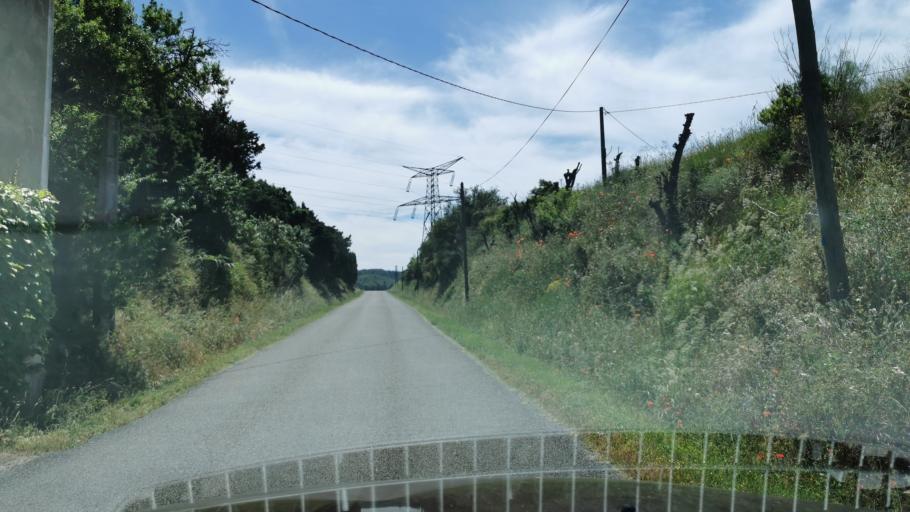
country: FR
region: Languedoc-Roussillon
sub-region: Departement de l'Aude
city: Nevian
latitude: 43.2016
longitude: 2.9026
